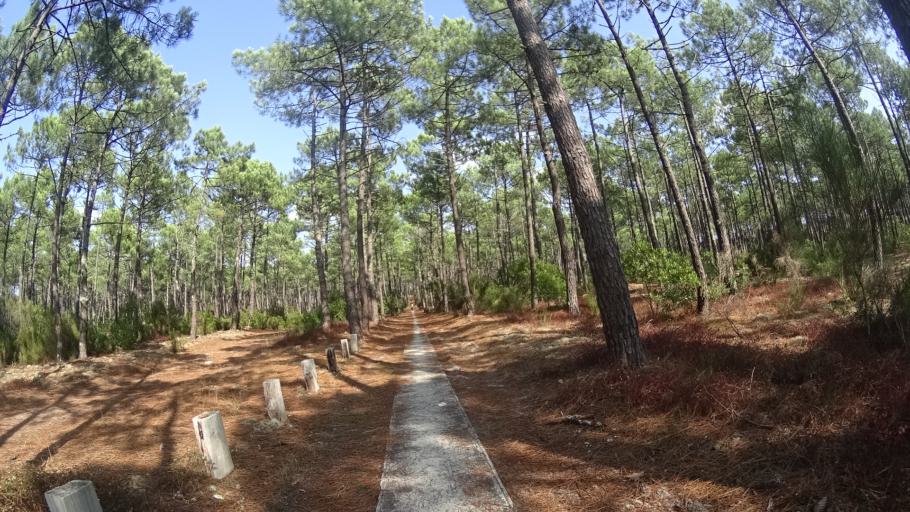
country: FR
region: Aquitaine
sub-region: Departement de la Gironde
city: Lacanau
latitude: 44.9633
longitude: -1.2001
